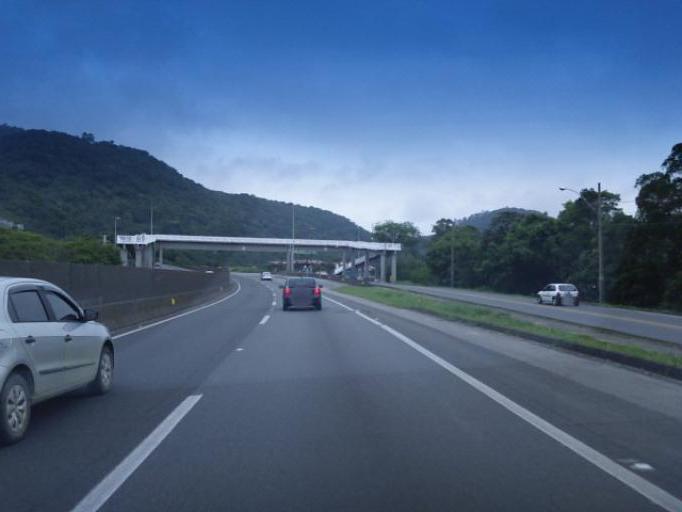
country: BR
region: Santa Catarina
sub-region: Itapema
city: Itapema
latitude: -27.0593
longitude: -48.5968
